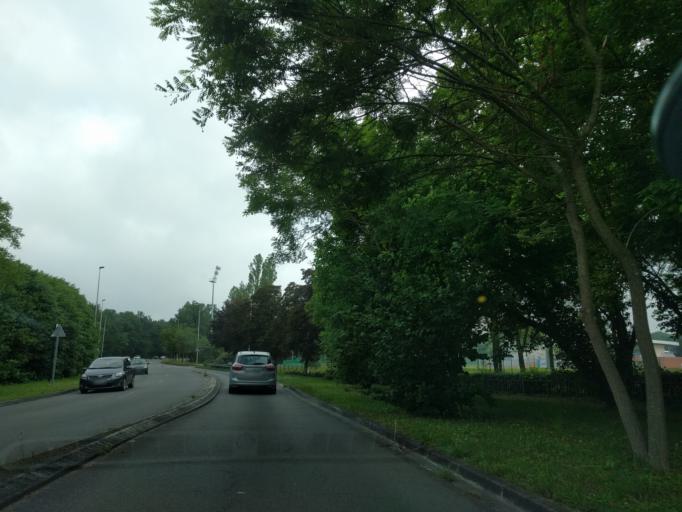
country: FR
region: Poitou-Charentes
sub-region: Departement de la Charente
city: Angouleme
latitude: 45.6314
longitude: 0.1450
